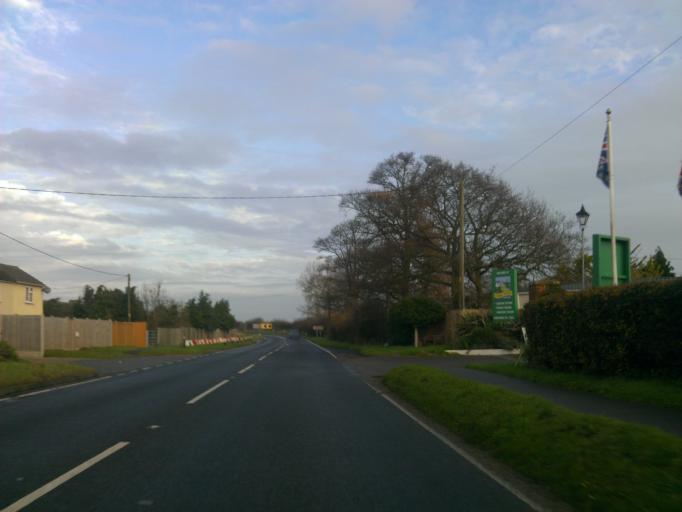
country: GB
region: England
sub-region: Essex
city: Saint Osyth
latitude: 51.8142
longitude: 1.0748
